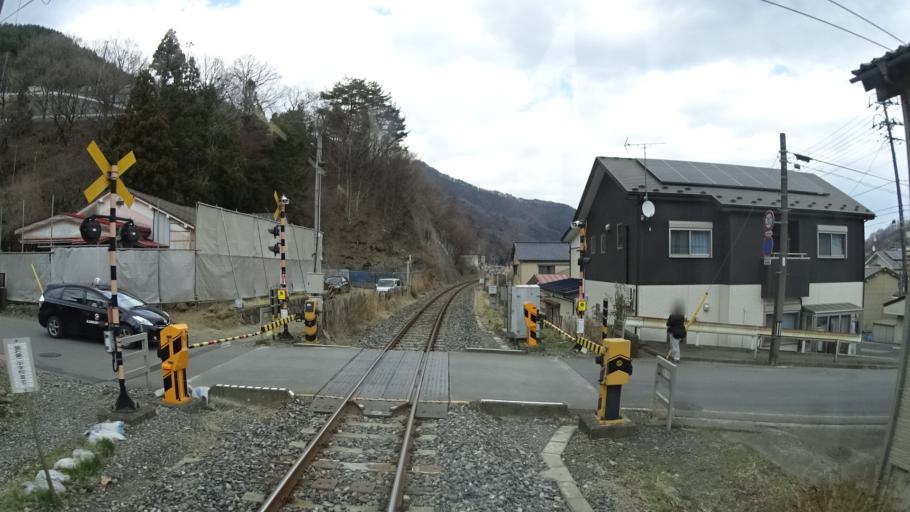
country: JP
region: Iwate
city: Kamaishi
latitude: 39.2715
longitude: 141.8566
